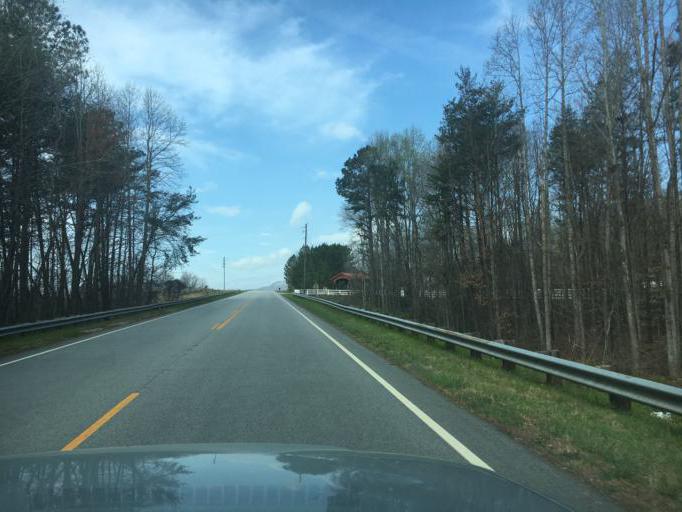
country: US
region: North Carolina
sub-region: Polk County
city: Tryon
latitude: 35.1246
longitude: -82.2606
